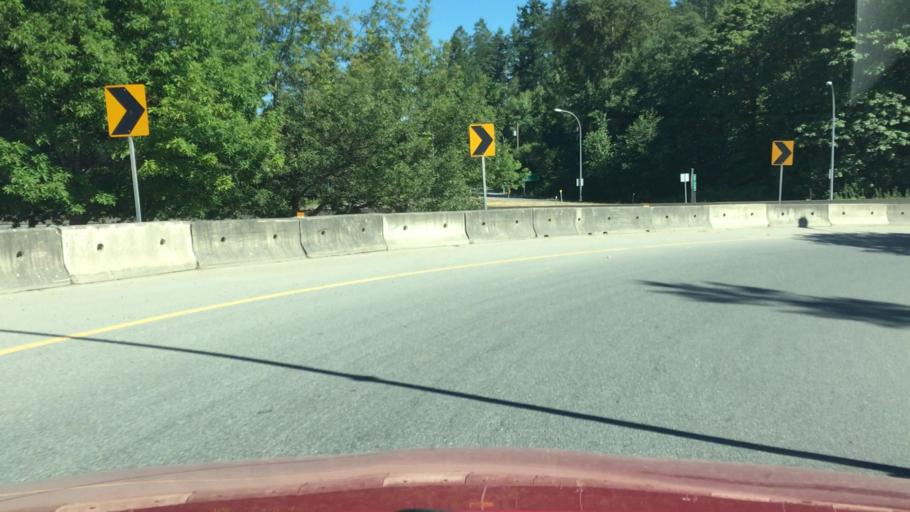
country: CA
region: British Columbia
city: North Saanich
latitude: 48.6766
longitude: -123.4273
